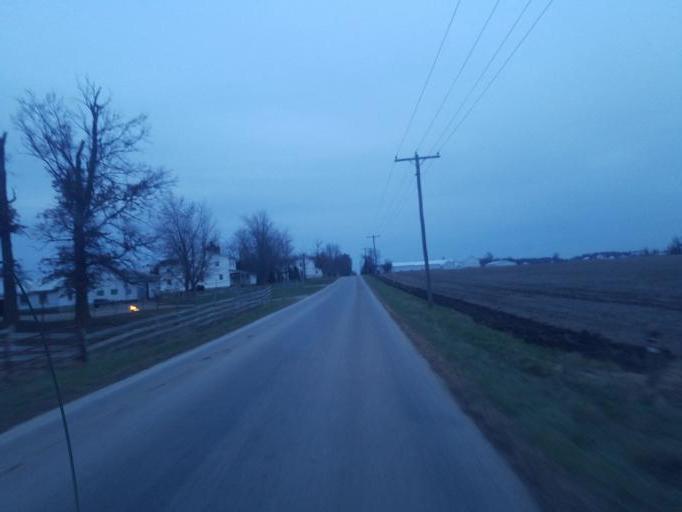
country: US
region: Indiana
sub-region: Adams County
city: Berne
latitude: 40.7315
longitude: -84.9321
